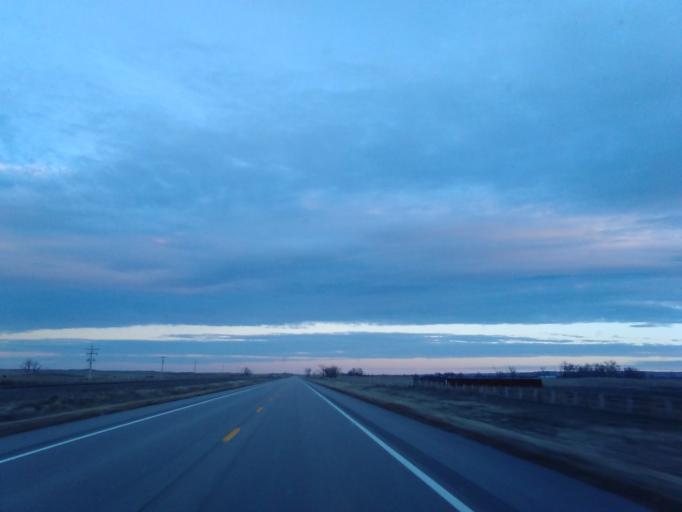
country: US
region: Nebraska
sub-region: Garden County
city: Oshkosh
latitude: 41.3912
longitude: -102.3008
